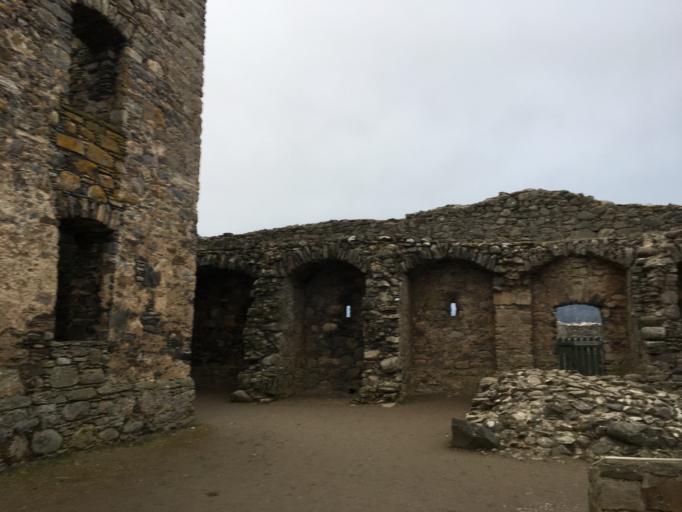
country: GB
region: Scotland
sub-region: Highland
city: Kingussie
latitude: 57.0721
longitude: -4.0392
